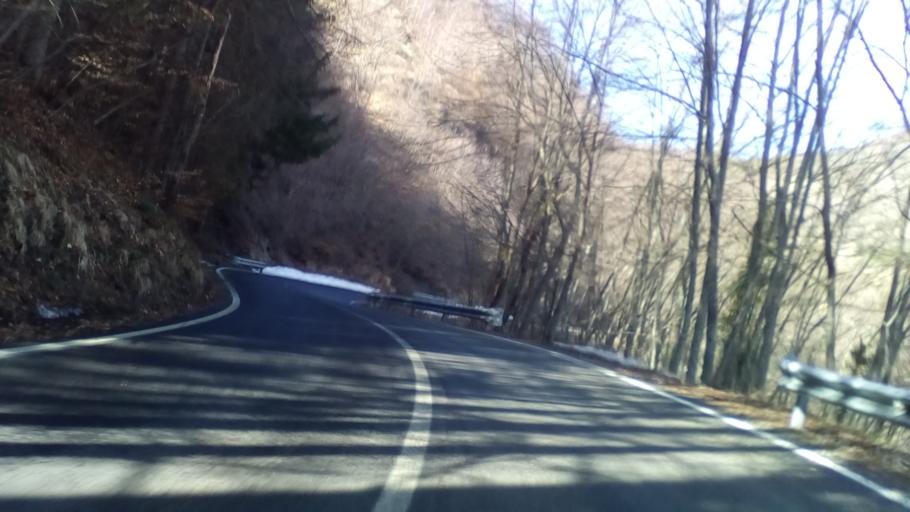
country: IT
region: Emilia-Romagna
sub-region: Provincia di Modena
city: Riolunato
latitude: 44.2513
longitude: 10.6310
